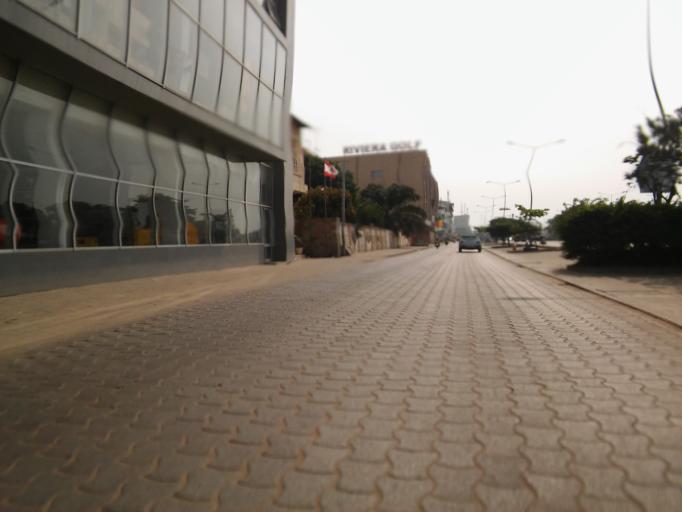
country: BJ
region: Littoral
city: Cotonou
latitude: 6.3621
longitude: 2.4463
